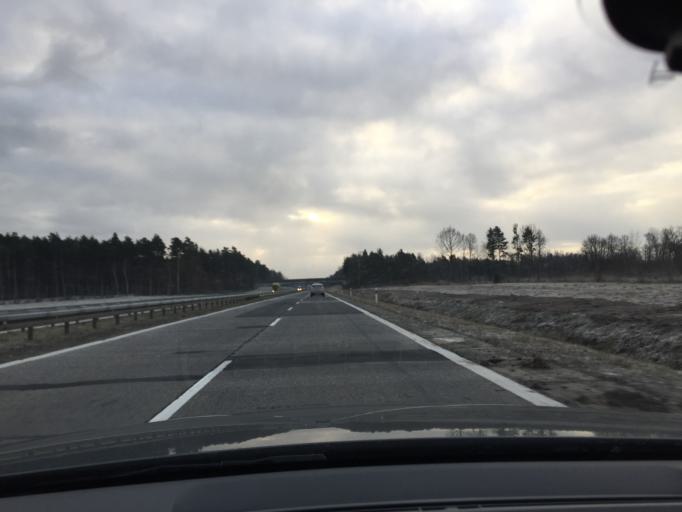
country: PL
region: Lubusz
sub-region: Powiat zarski
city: Lipinki Luzyckie
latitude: 51.5797
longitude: 15.0264
